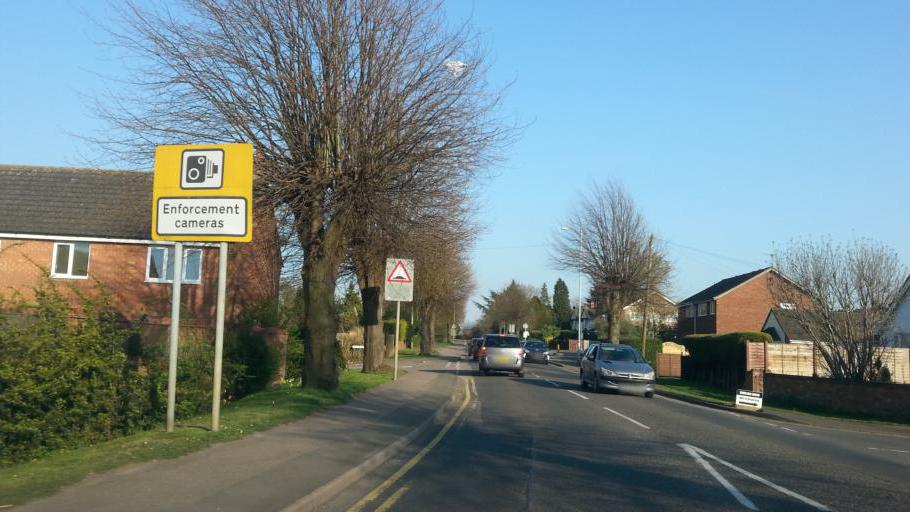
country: GB
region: England
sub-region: Northamptonshire
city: Rushden
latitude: 52.2955
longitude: -0.6200
